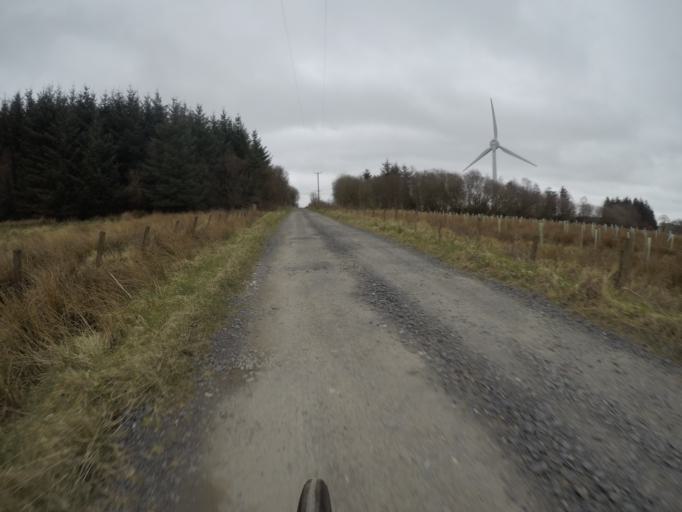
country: GB
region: Scotland
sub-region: East Ayrshire
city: Newmilns
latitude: 55.6280
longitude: -4.3424
